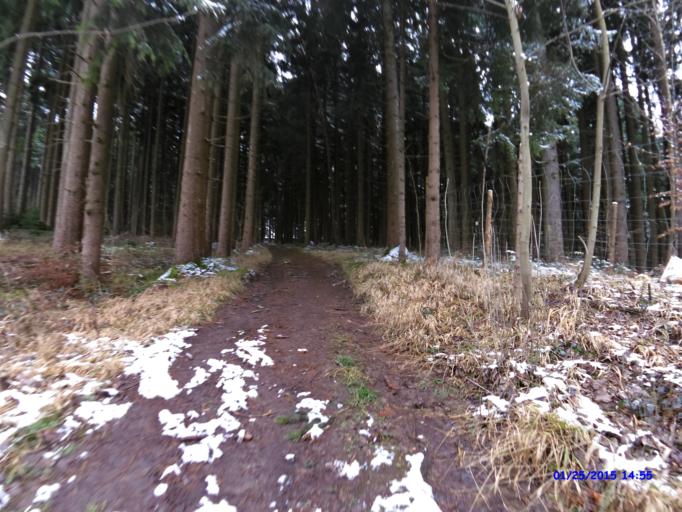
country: DE
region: Bavaria
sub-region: Lower Bavaria
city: Eching
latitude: 48.4991
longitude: 12.0794
